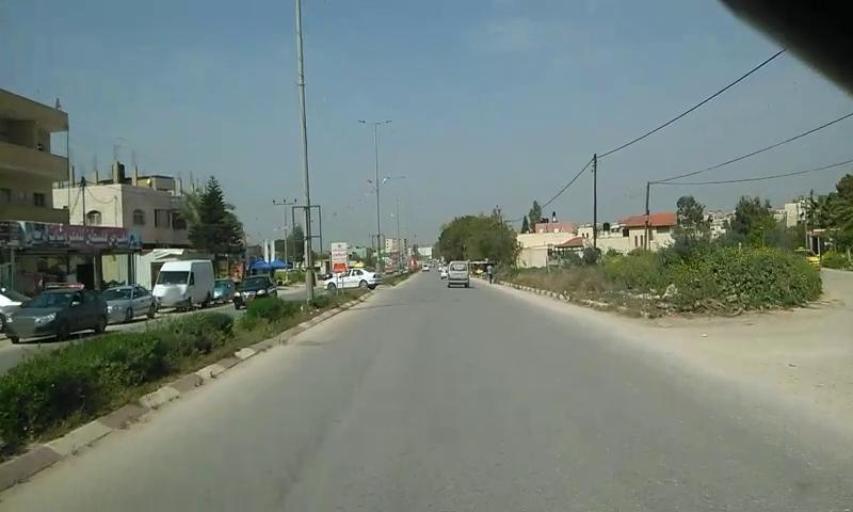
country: PS
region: West Bank
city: Janin
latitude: 32.4734
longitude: 35.3022
